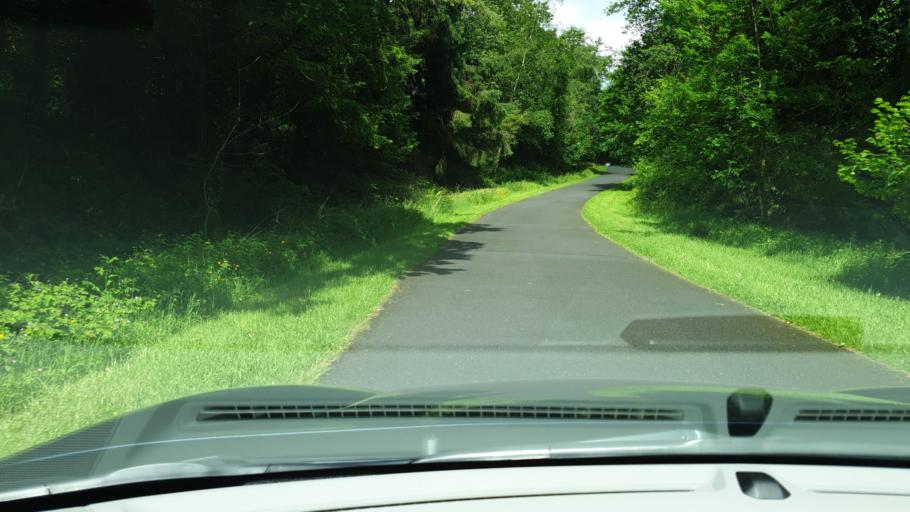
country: IE
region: Ulster
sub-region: An Cabhan
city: Kingscourt
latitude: 53.9154
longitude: -6.7889
